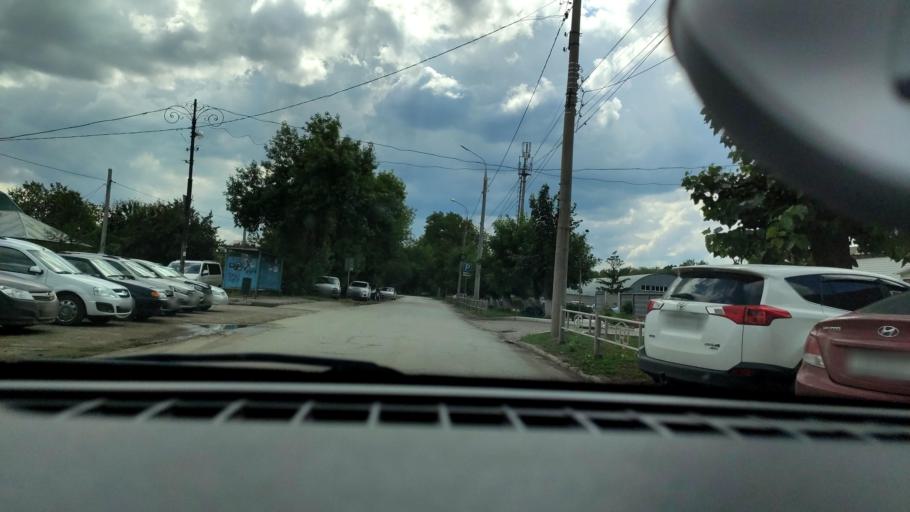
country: RU
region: Samara
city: Novokuybyshevsk
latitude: 53.1051
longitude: 50.0387
